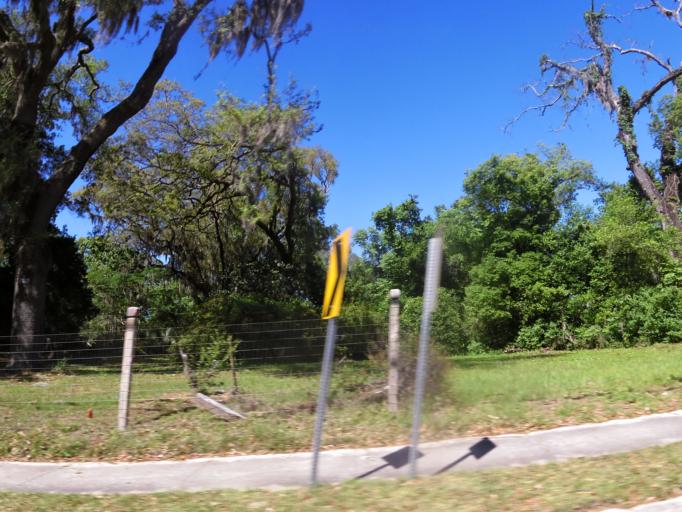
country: US
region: Florida
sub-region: Duval County
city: Jacksonville
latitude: 30.3202
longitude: -81.5799
